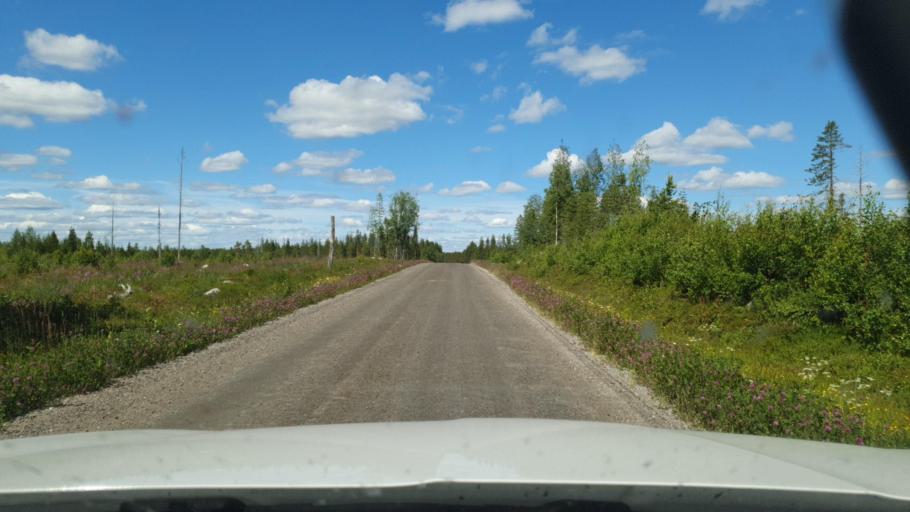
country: SE
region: Vaesterbotten
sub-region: Skelleftea Kommun
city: Byske
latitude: 65.1354
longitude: 21.1899
